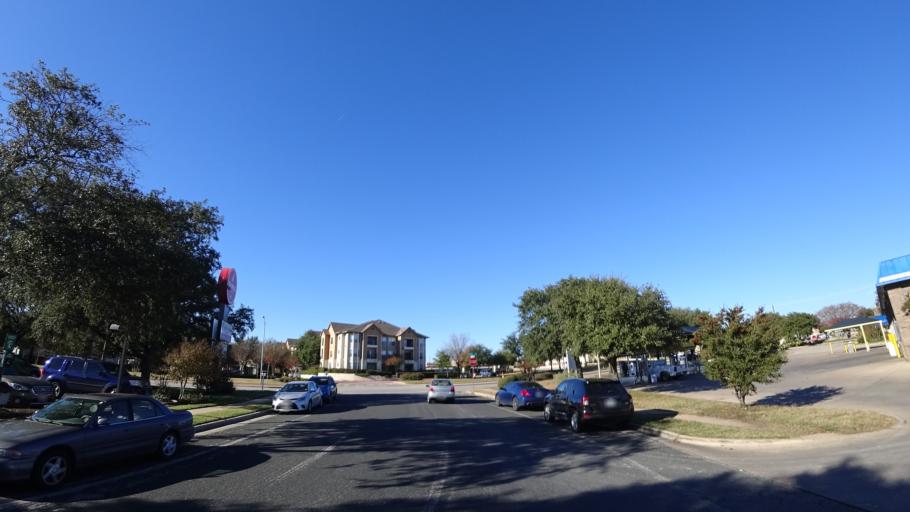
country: US
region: Texas
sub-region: Travis County
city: Wells Branch
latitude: 30.4116
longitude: -97.6913
